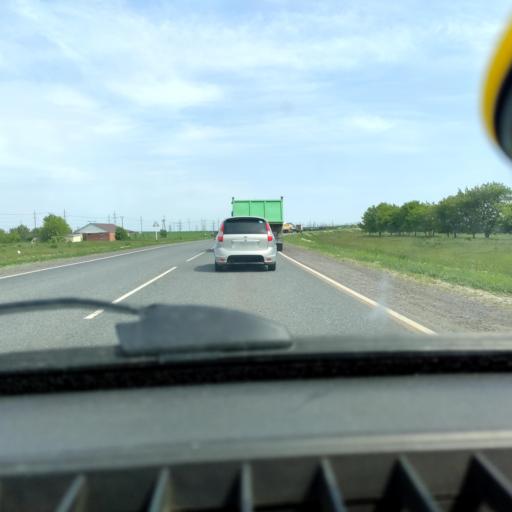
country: RU
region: Samara
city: Povolzhskiy
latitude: 53.6410
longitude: 49.6617
